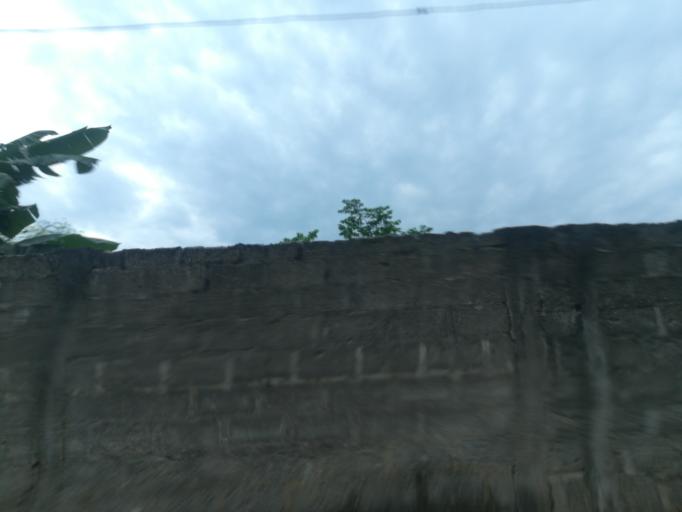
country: NG
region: Rivers
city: Port Harcourt
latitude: 4.8020
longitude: 6.9531
